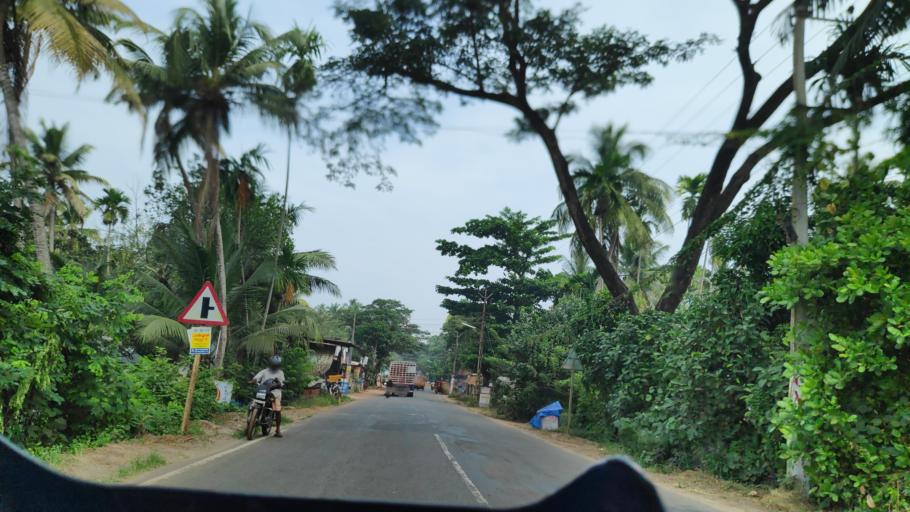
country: IN
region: Kerala
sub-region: Alappuzha
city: Shertallai
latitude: 9.7082
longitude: 76.3574
